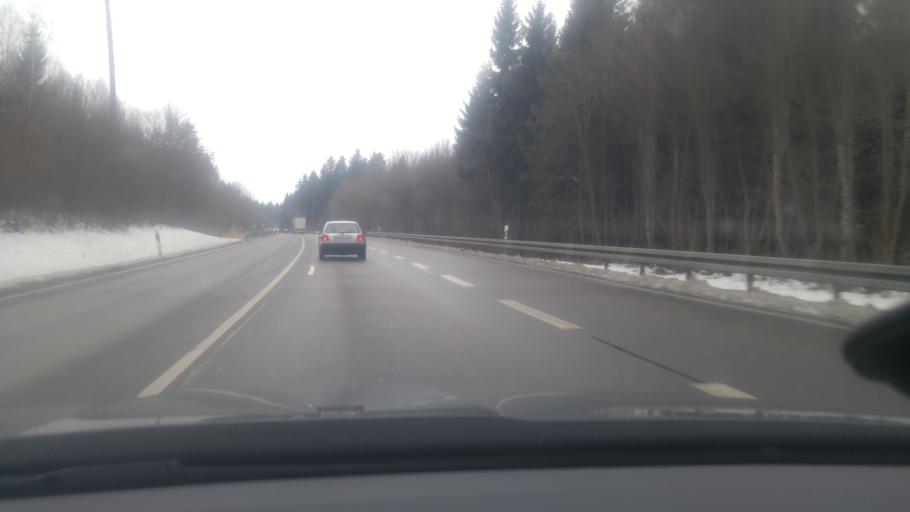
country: DE
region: Baden-Wuerttemberg
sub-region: Freiburg Region
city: Bad Durrheim
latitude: 48.0446
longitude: 8.5377
